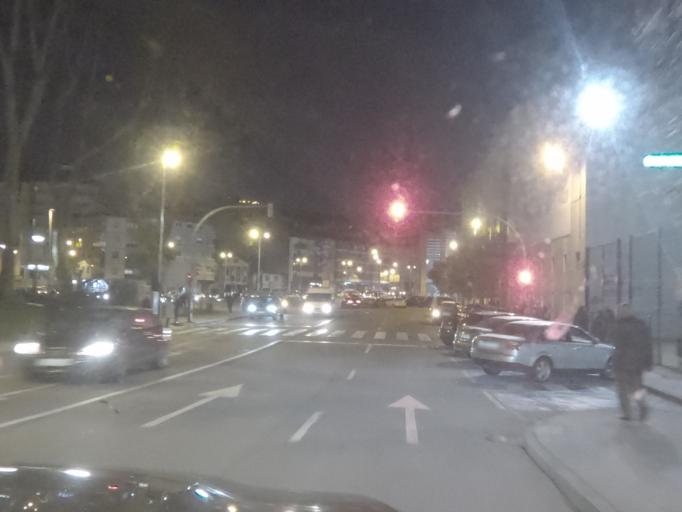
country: ES
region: Galicia
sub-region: Provincia de Ourense
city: Ourense
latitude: 42.3434
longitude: -7.8695
